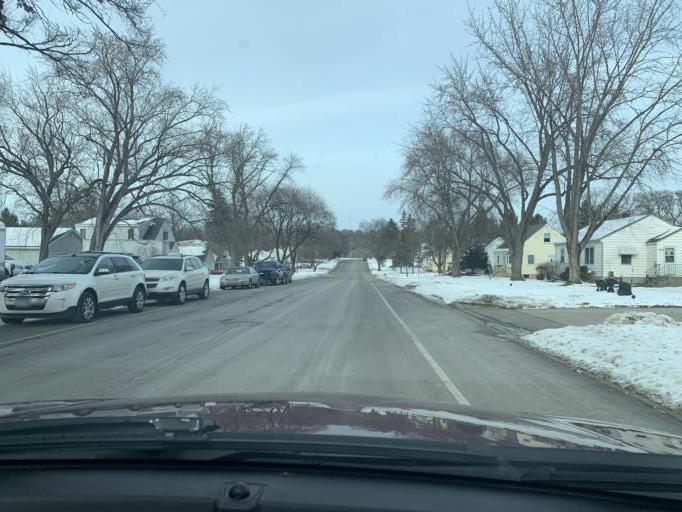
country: US
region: Minnesota
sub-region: Washington County
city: Saint Paul Park
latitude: 44.8412
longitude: -92.9841
